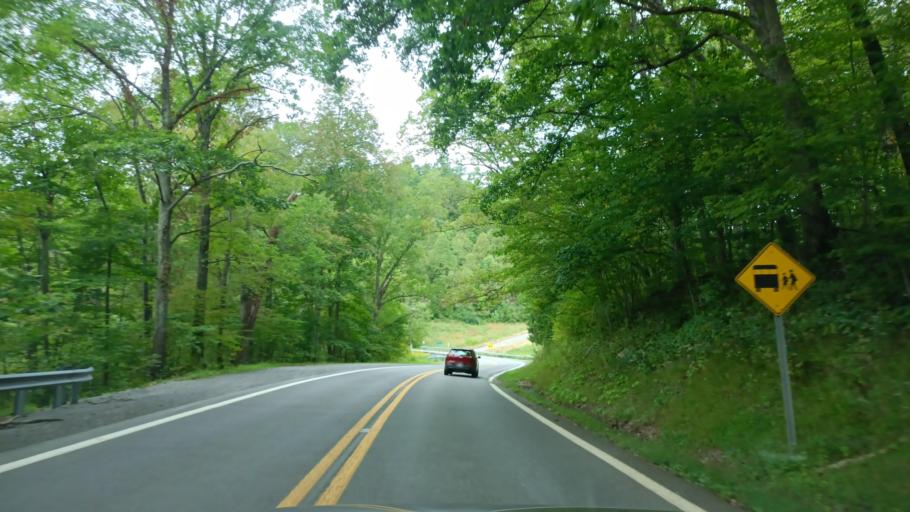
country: US
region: West Virginia
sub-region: Taylor County
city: Grafton
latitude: 39.3362
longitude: -79.8998
